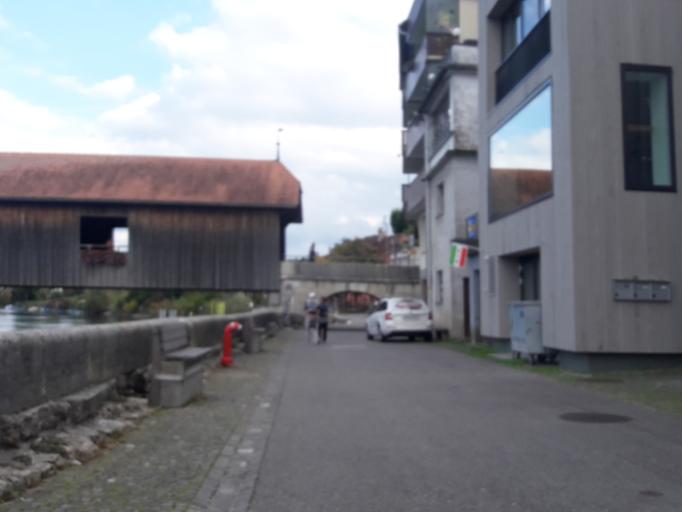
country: CH
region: Bern
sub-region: Biel/Bienne District
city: Meinisberg
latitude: 47.1404
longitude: 7.3717
